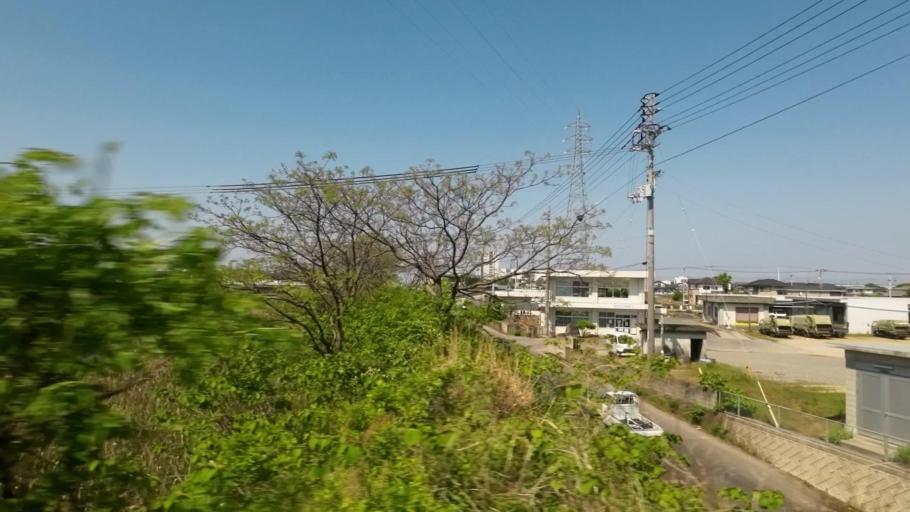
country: JP
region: Kagawa
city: Kan'onjicho
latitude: 34.1168
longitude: 133.6476
